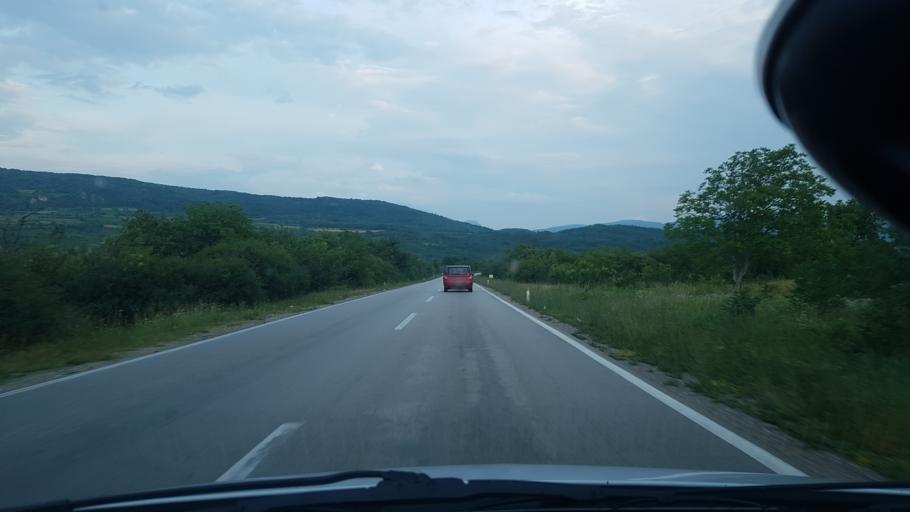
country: RS
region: Central Serbia
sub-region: Nisavski Okrug
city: Niska Banja
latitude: 43.3522
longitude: 22.0371
